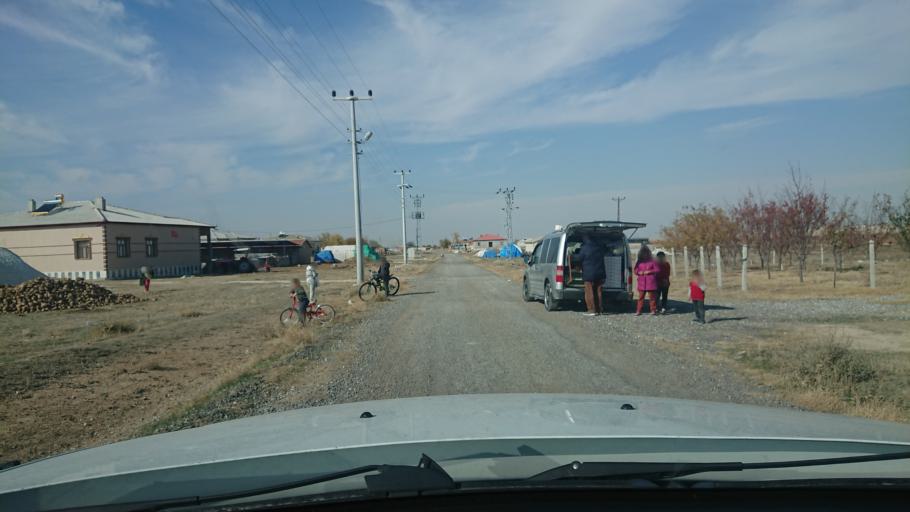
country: TR
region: Aksaray
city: Sultanhani
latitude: 38.2549
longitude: 33.4798
